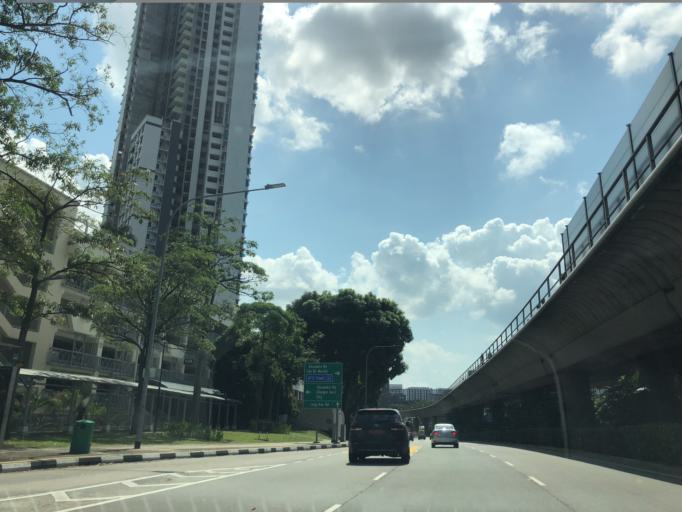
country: SG
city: Singapore
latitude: 1.2933
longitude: 103.8071
